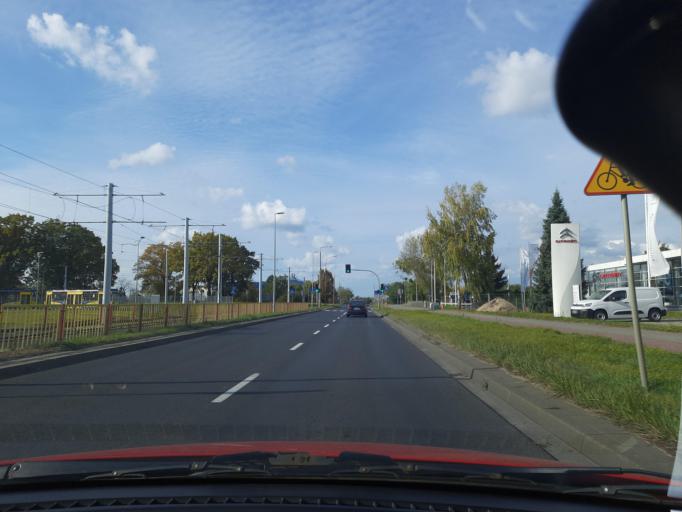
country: PL
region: Kujawsko-Pomorskie
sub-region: Powiat torunski
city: Wielka Nieszawka
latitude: 53.0157
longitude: 18.5481
